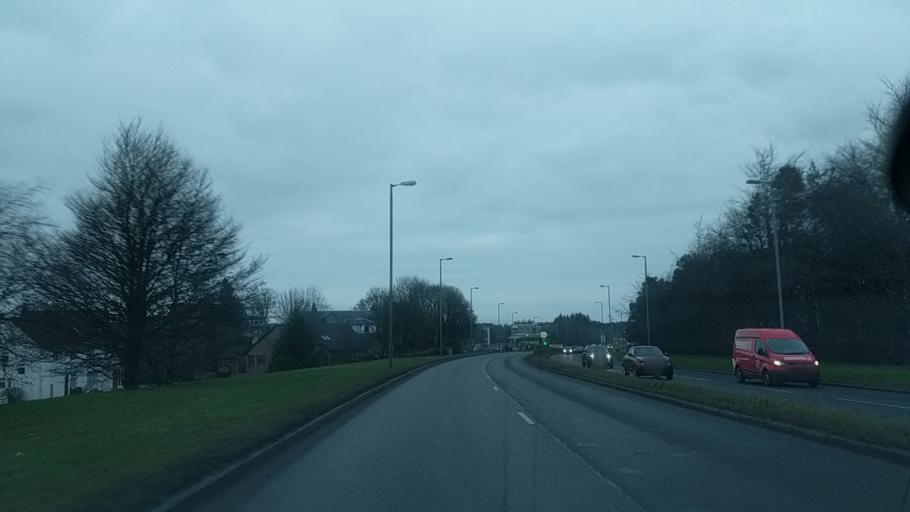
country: GB
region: Scotland
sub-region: South Lanarkshire
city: East Kilbride
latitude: 55.7650
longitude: -4.1664
